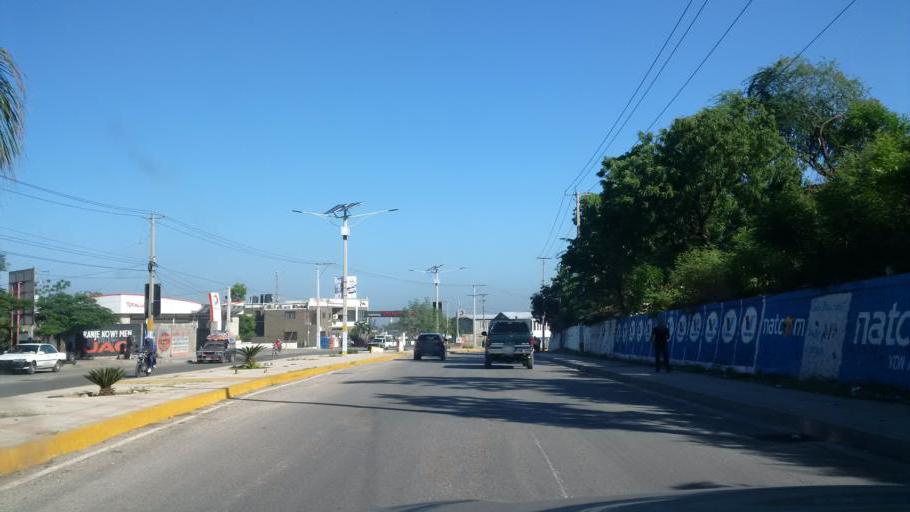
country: HT
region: Ouest
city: Delmas 73
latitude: 18.5580
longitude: -72.3178
